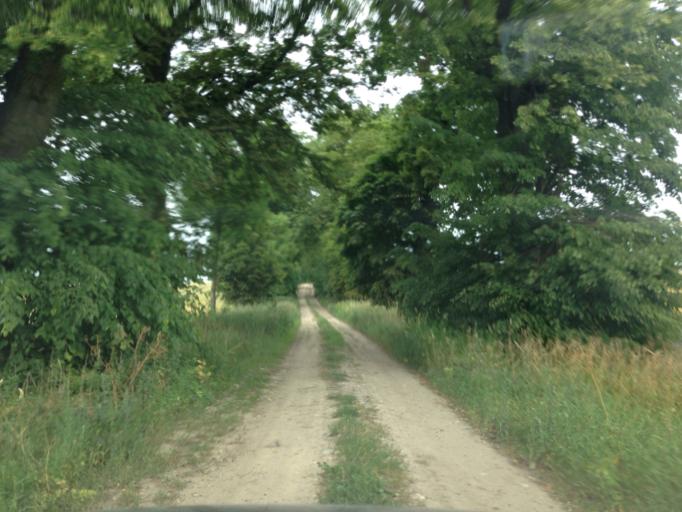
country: PL
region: Kujawsko-Pomorskie
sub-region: Powiat brodnicki
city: Bobrowo
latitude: 53.2116
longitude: 19.2466
